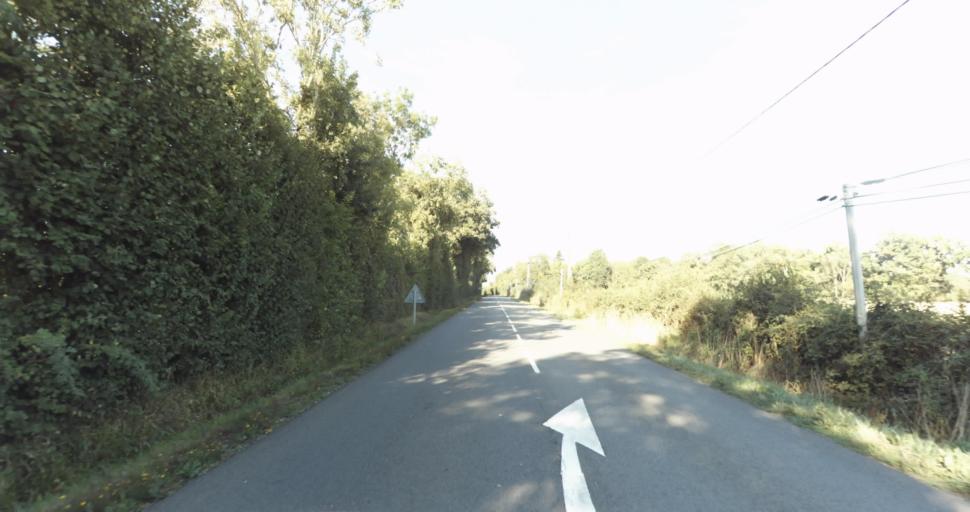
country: FR
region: Lower Normandy
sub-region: Departement de l'Orne
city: Vimoutiers
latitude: 48.9015
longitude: 0.1358
